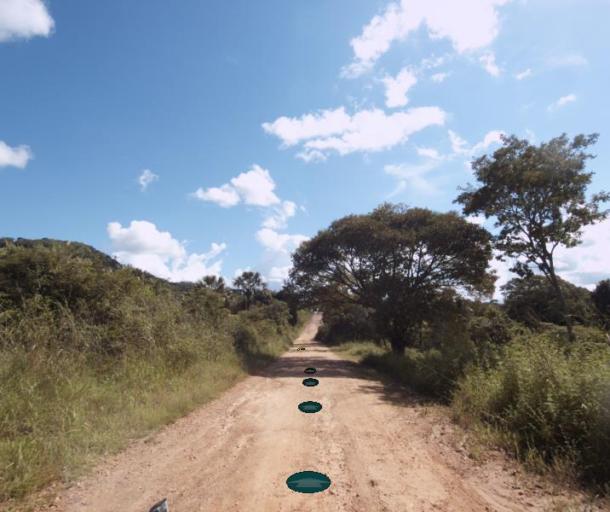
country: BR
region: Goias
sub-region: Pirenopolis
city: Pirenopolis
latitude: -15.7834
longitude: -49.0533
